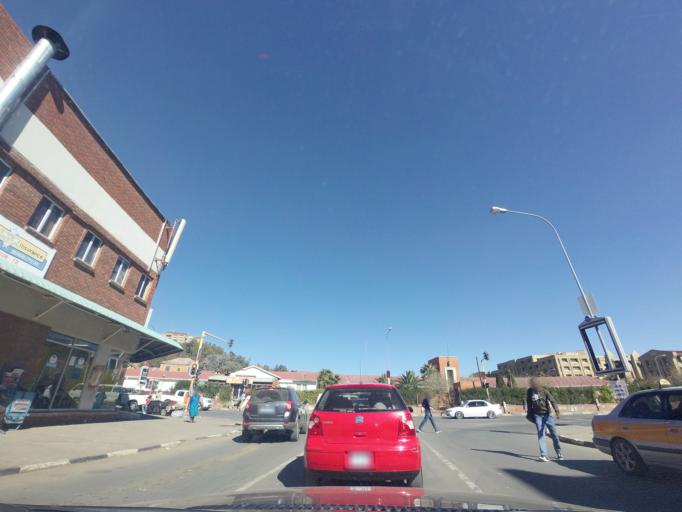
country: LS
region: Maseru
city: Maseru
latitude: -29.3148
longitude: 27.4870
